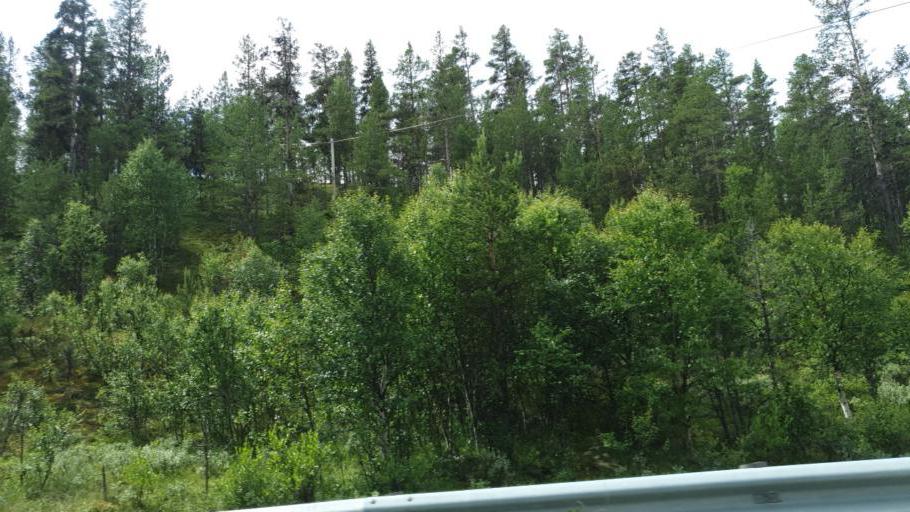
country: NO
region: Oppland
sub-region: Vaga
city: Vagamo
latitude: 61.7127
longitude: 9.0523
